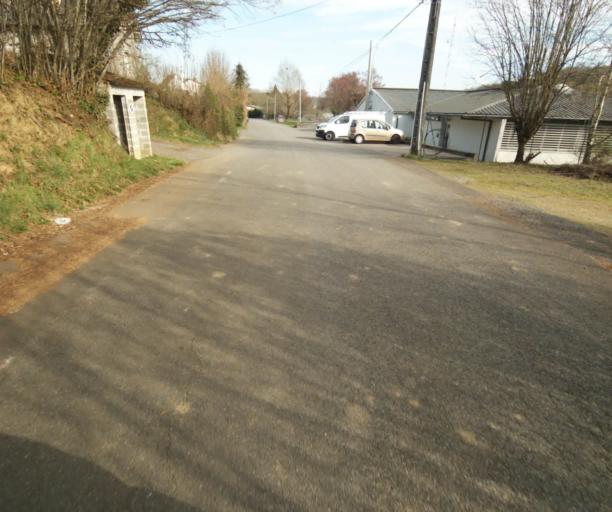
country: FR
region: Limousin
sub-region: Departement de la Correze
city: Tulle
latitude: 45.2890
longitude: 1.7619
